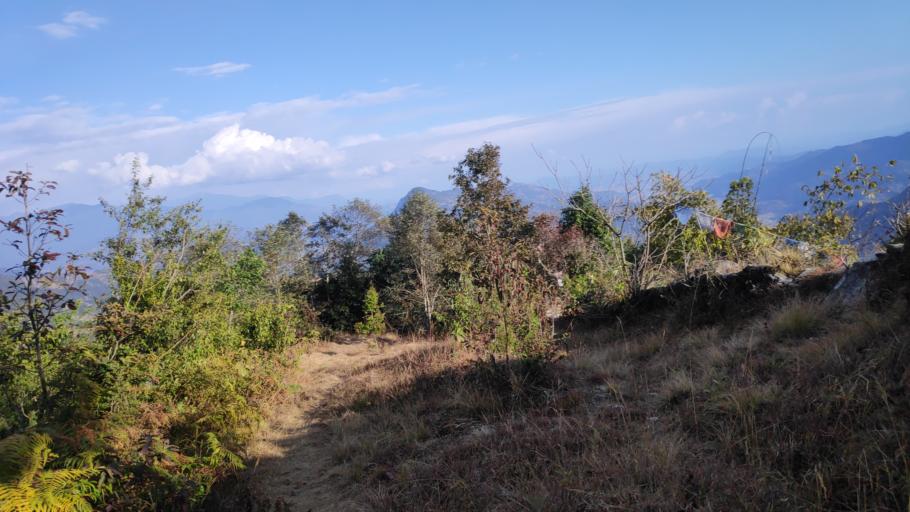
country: NP
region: Western Region
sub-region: Gandaki Zone
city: Pokhara
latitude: 28.2889
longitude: 83.8301
